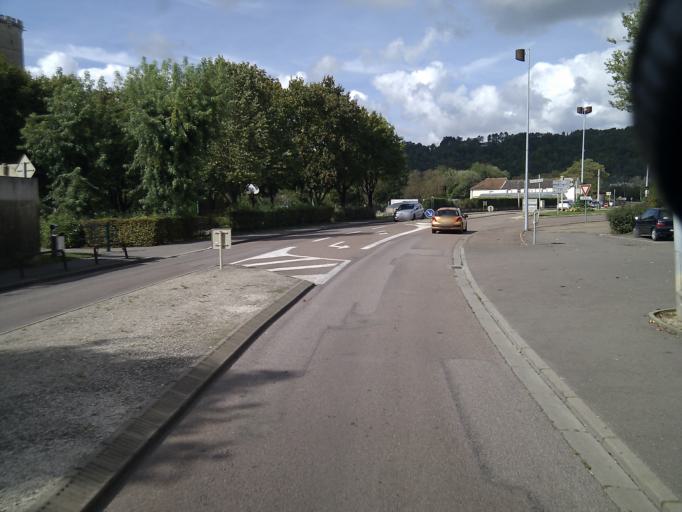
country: FR
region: Bourgogne
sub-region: Departement de la Cote-d'Or
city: Montbard
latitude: 47.6268
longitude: 4.3389
